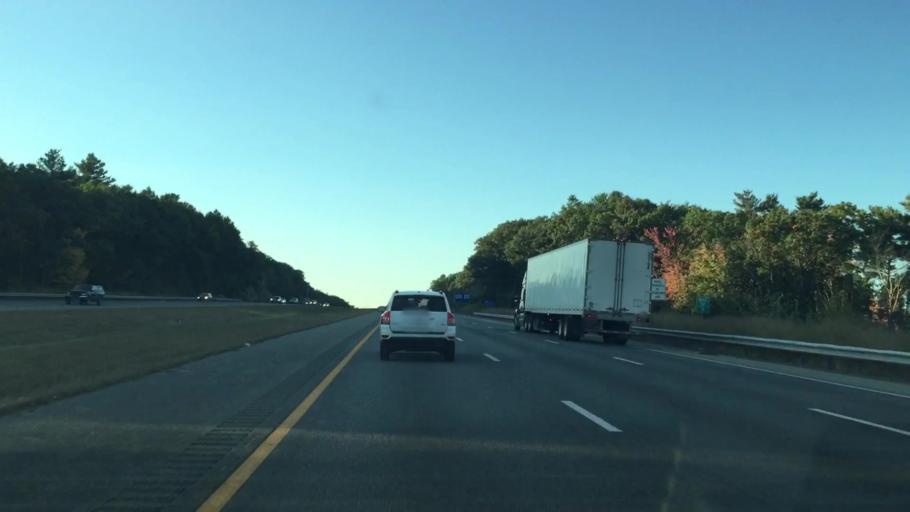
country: US
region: Massachusetts
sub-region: Middlesex County
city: Burlington
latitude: 42.4888
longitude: -71.2297
